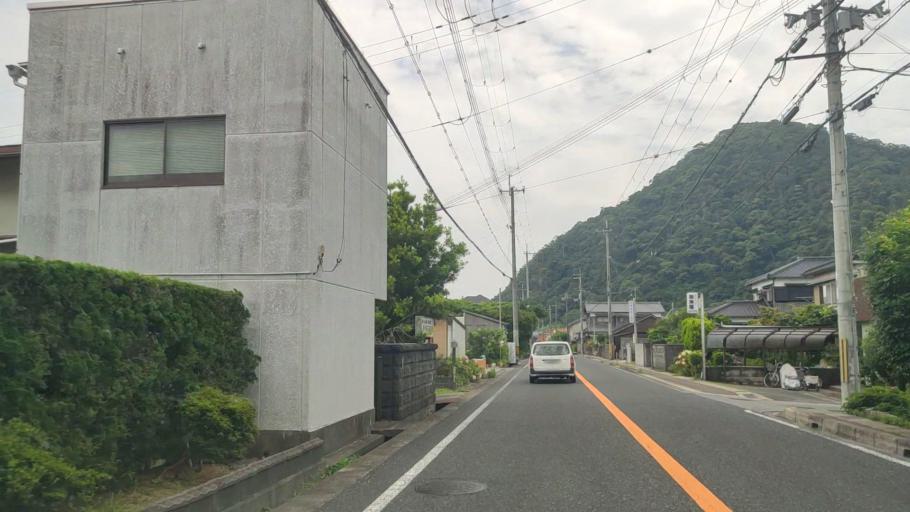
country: JP
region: Hyogo
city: Tatsunocho-tominaga
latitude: 34.8785
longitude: 134.5463
